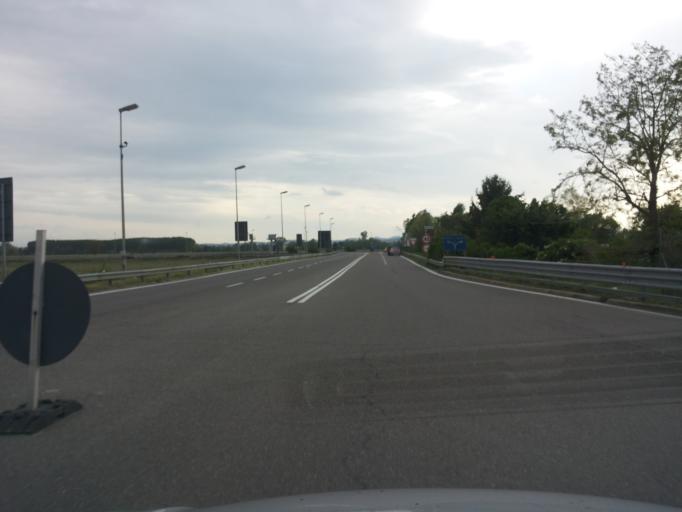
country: IT
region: Piedmont
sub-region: Provincia di Alessandria
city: Villanova Monferrato
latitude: 45.1637
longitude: 8.4844
